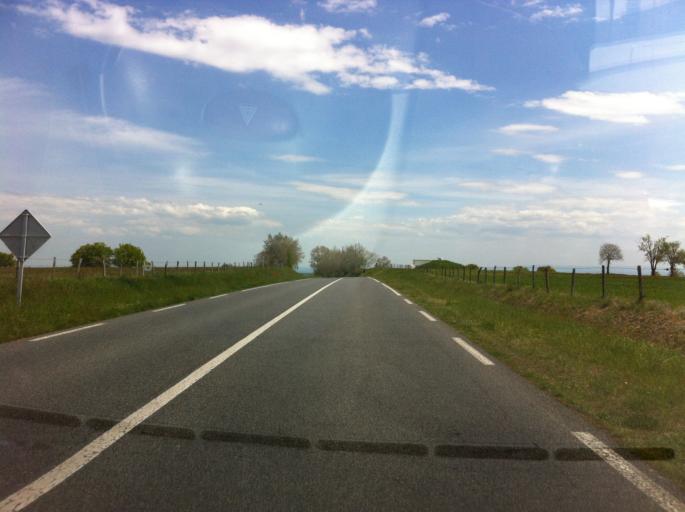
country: FR
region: Auvergne
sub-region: Departement de l'Allier
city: Chantelle
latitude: 46.3174
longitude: 3.1297
